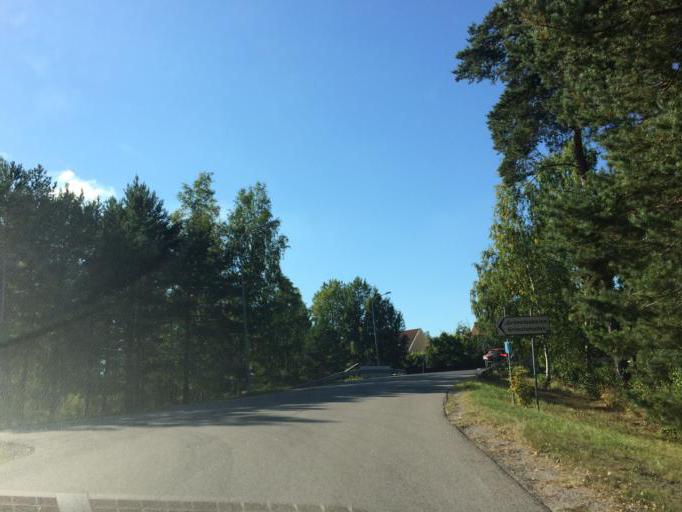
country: SE
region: Stockholm
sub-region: Upplands Vasby Kommun
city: Upplands Vaesby
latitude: 59.5013
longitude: 17.9487
